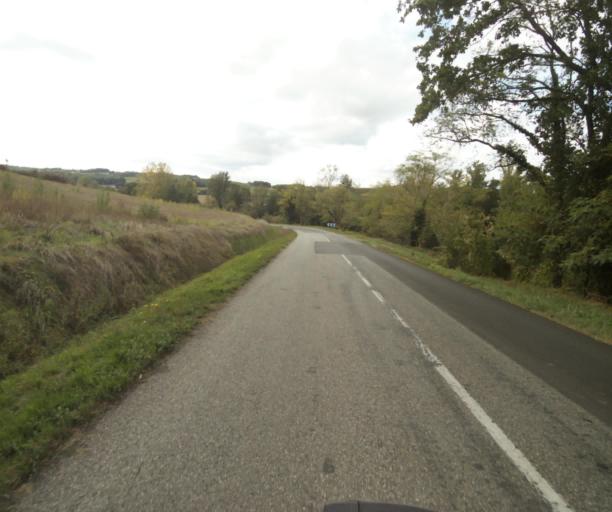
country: FR
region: Midi-Pyrenees
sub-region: Departement du Tarn-et-Garonne
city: Verdun-sur-Garonne
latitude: 43.8537
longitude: 1.1327
